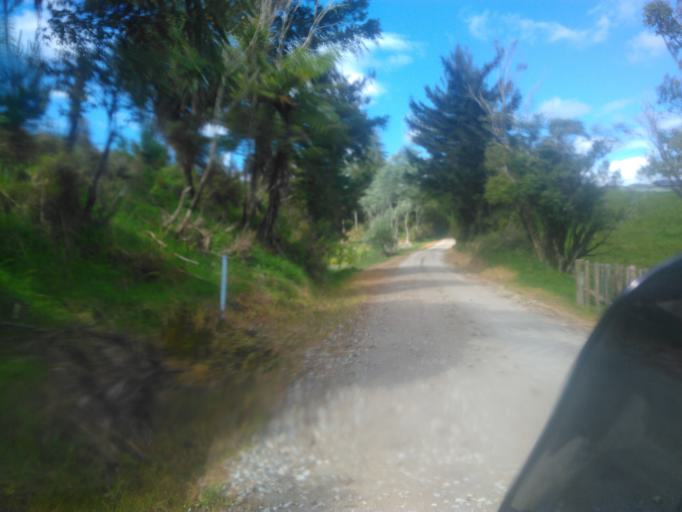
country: NZ
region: Hawke's Bay
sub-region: Wairoa District
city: Wairoa
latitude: -38.7763
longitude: 177.6306
